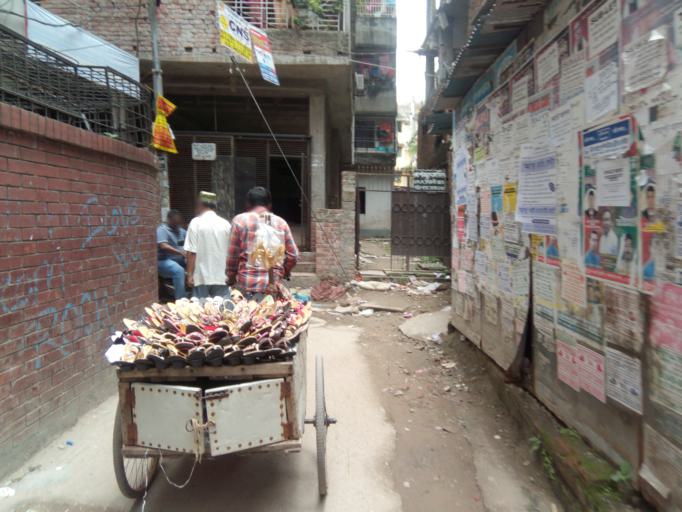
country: BD
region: Dhaka
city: Azimpur
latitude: 23.7456
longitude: 90.3880
